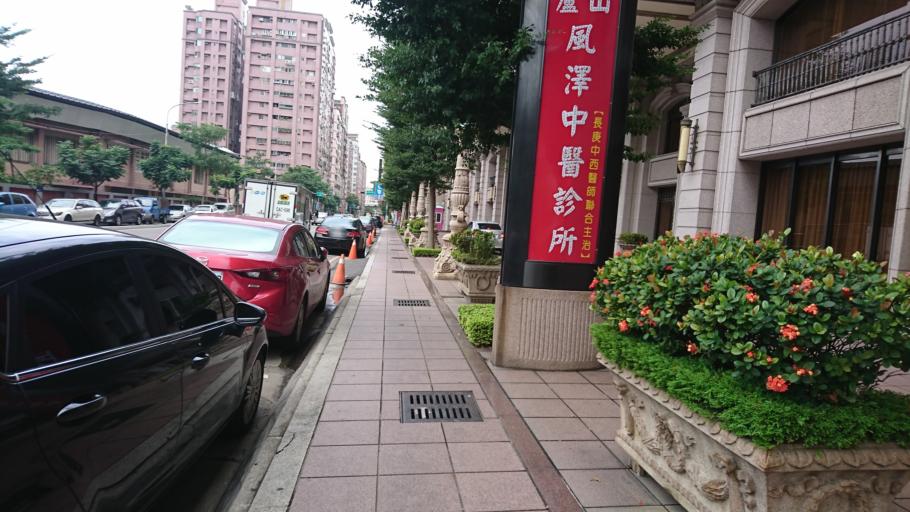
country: TW
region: Taiwan
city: Taoyuan City
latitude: 25.0541
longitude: 121.2995
